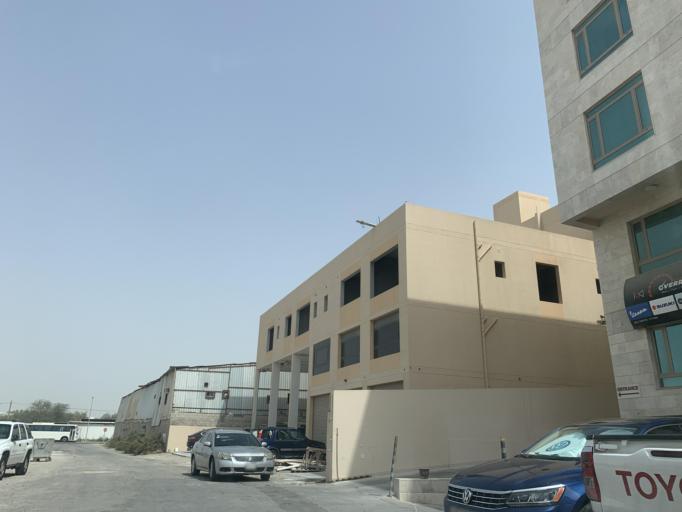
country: BH
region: Northern
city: Madinat `Isa
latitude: 26.1870
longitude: 50.5237
